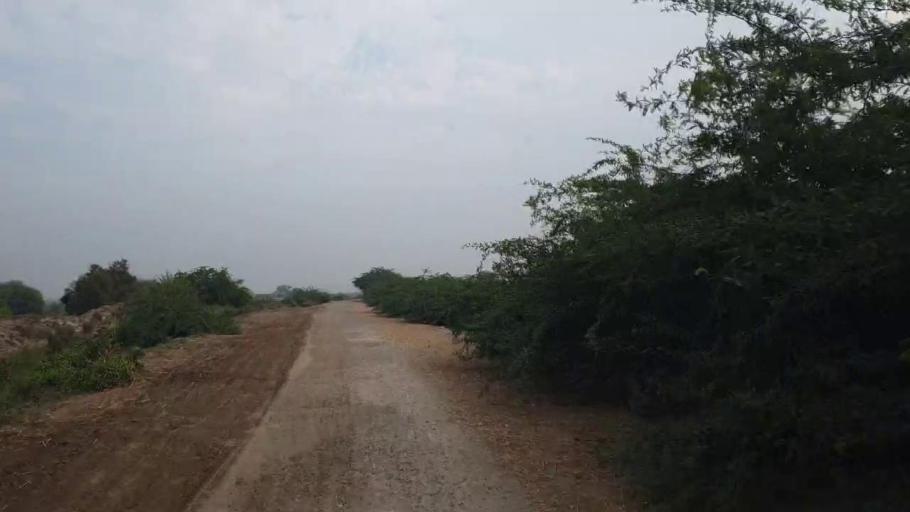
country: PK
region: Sindh
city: Talhar
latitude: 24.8093
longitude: 68.8736
